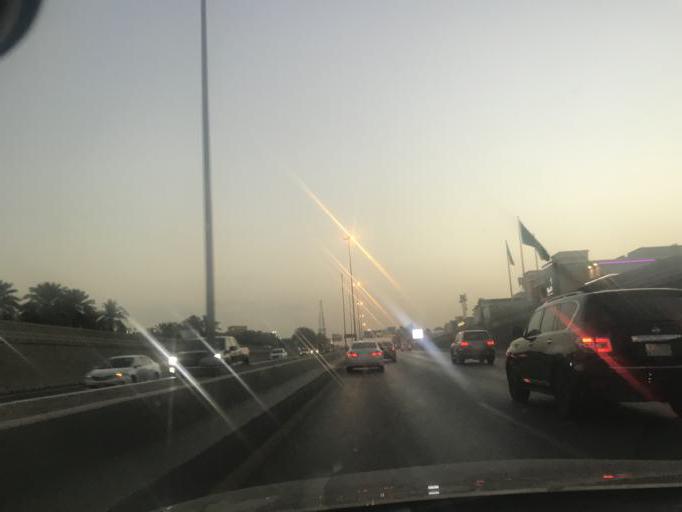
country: SA
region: Ar Riyad
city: Riyadh
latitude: 24.6753
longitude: 46.6763
